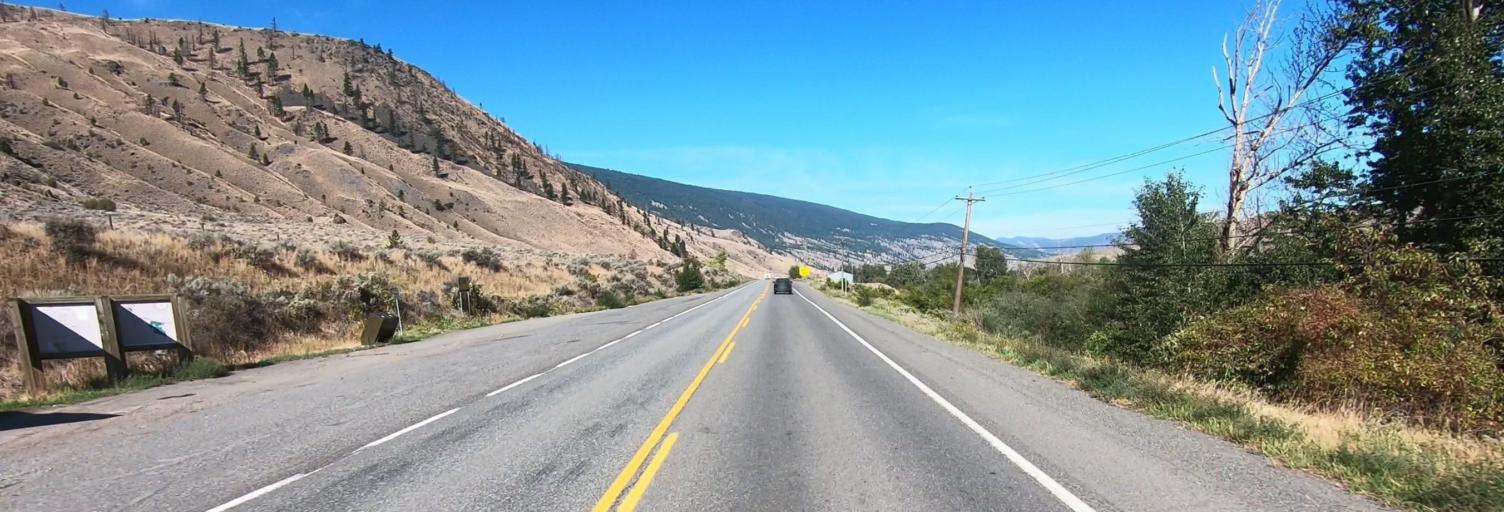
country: CA
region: British Columbia
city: Cache Creek
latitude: 50.8221
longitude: -121.3370
